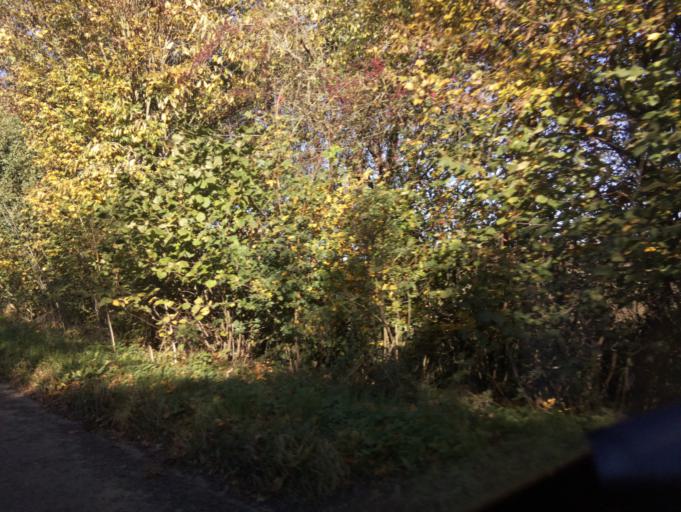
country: GB
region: England
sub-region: Somerset
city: Stoke-sub-Hamdon
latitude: 50.9746
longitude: -2.7266
